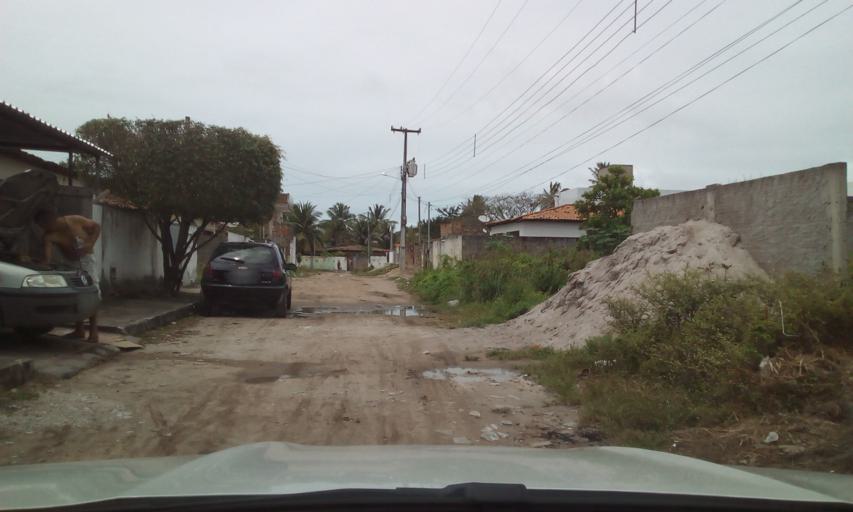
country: BR
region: Paraiba
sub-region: Conde
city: Conde
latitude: -7.2172
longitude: -34.8402
